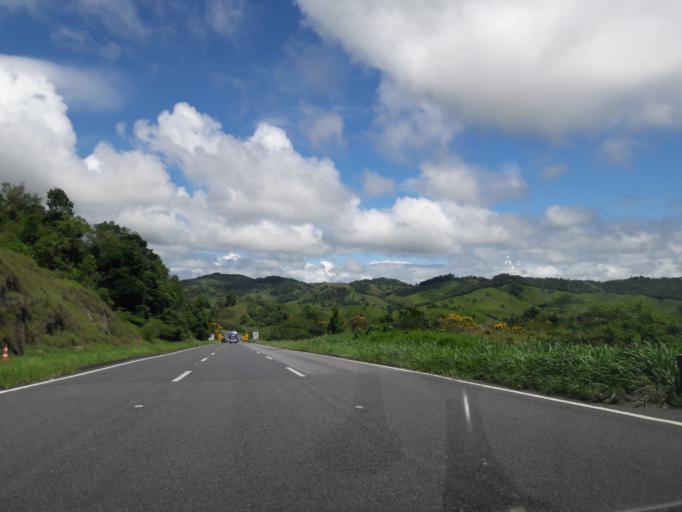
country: BR
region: Sao Paulo
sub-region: Cajati
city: Cajati
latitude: -24.9548
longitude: -48.4574
